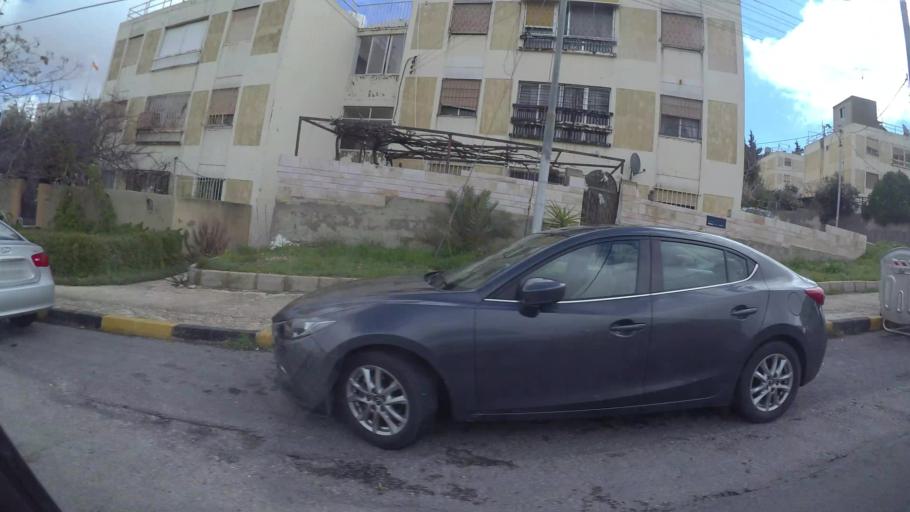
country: JO
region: Amman
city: Al Jubayhah
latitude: 32.0615
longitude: 35.8842
